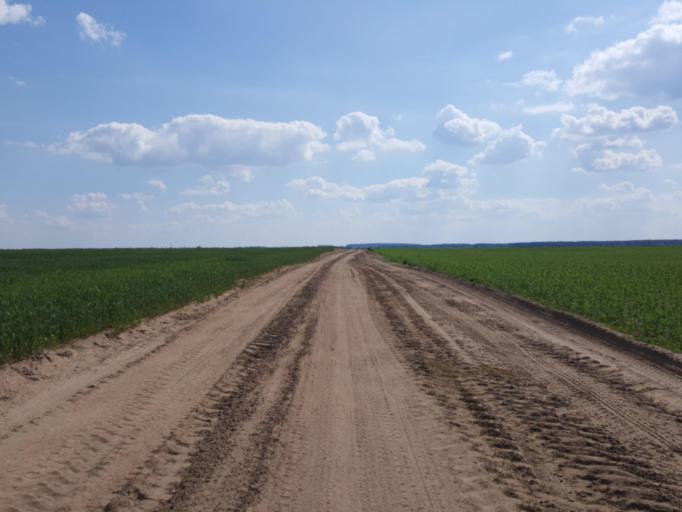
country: BY
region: Brest
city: Kamyanyuki
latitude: 52.4928
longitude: 23.6011
